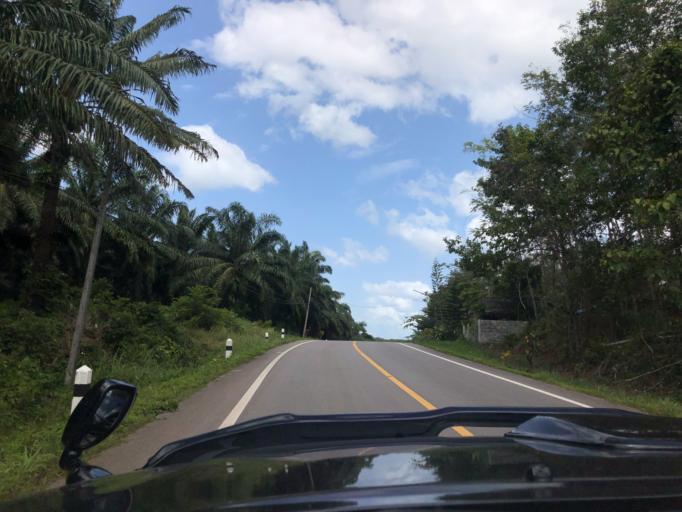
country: TH
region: Krabi
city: Khlong Thom
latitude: 7.9476
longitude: 99.2083
